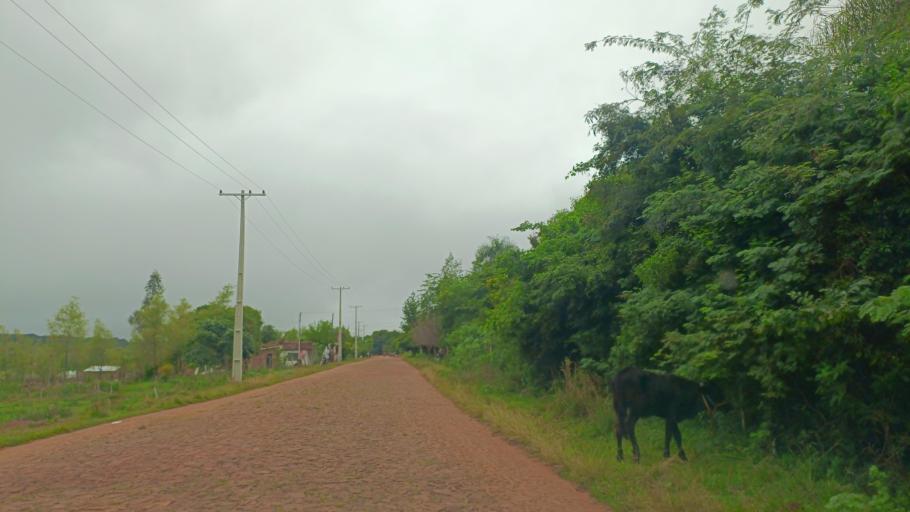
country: PY
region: Misiones
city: Santa Maria
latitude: -26.8736
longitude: -57.0061
